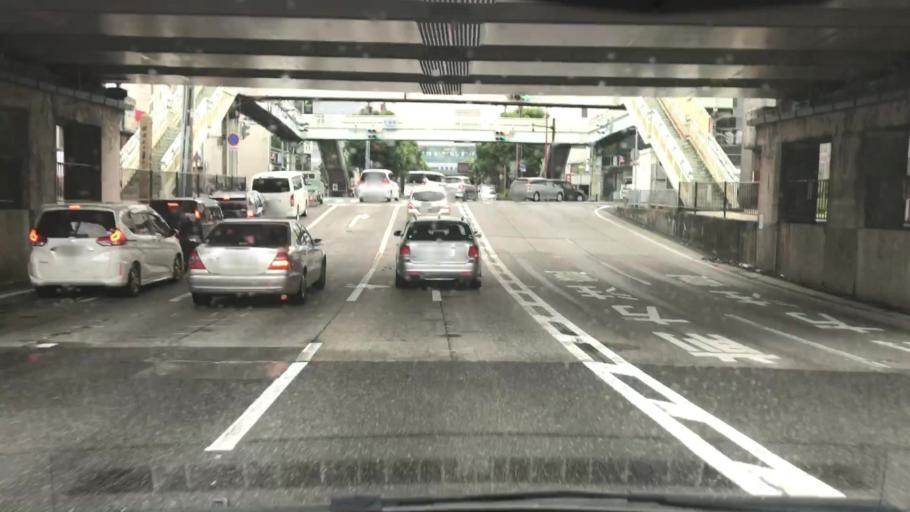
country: JP
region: Hyogo
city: Nishinomiya-hama
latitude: 34.7393
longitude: 135.3394
